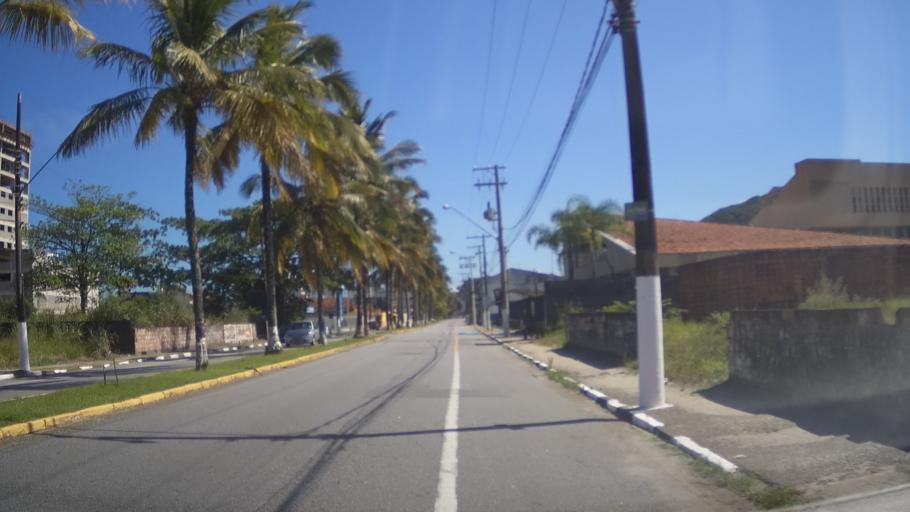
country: BR
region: Sao Paulo
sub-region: Mongagua
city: Mongagua
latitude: -24.0885
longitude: -46.6084
